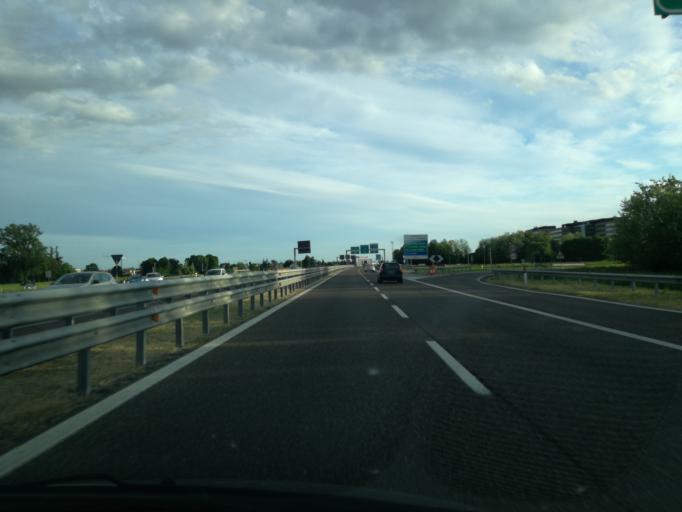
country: IT
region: Lombardy
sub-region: Provincia di Monza e Brianza
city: Agrate Brianza
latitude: 45.5774
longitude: 9.3422
